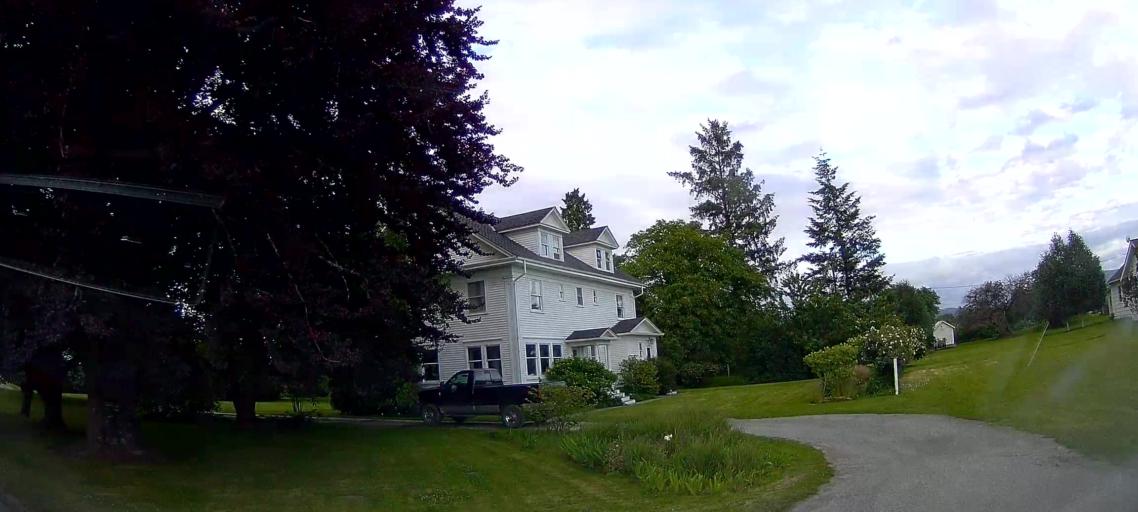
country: US
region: Washington
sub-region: Skagit County
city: Mount Vernon
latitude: 48.3404
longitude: -122.3900
